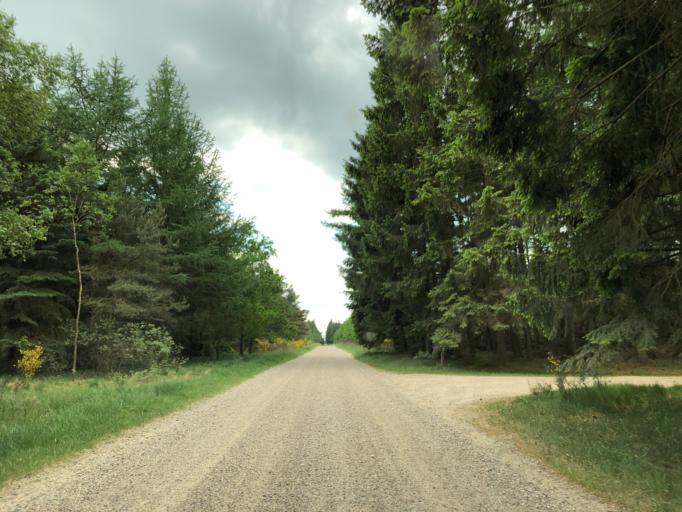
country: DK
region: Central Jutland
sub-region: Struer Kommune
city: Struer
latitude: 56.4547
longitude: 8.4411
